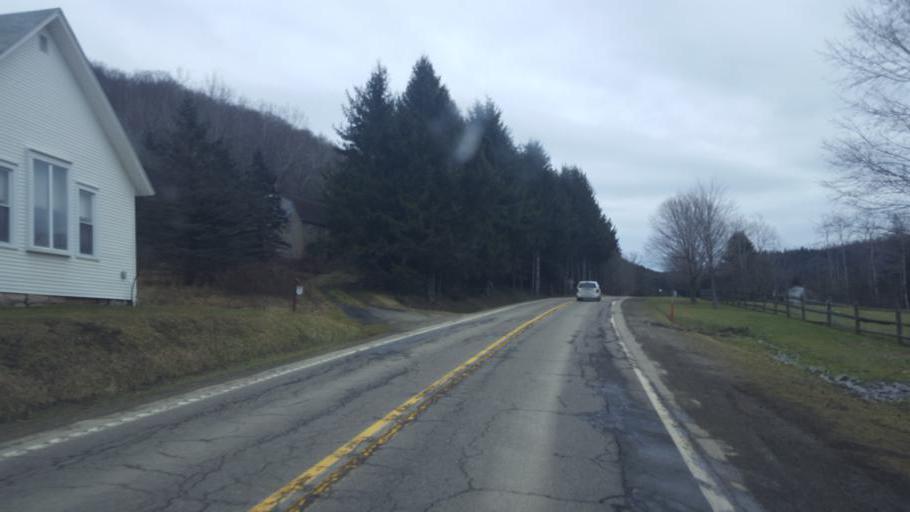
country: US
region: Pennsylvania
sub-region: Potter County
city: Coudersport
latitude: 41.8149
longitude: -78.0066
